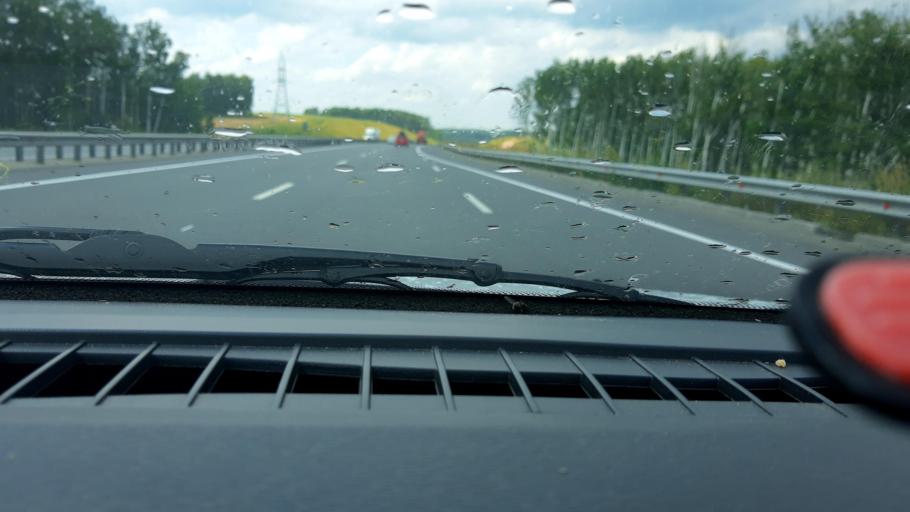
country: RU
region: Nizjnij Novgorod
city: Kstovo
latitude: 56.0678
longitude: 44.1180
